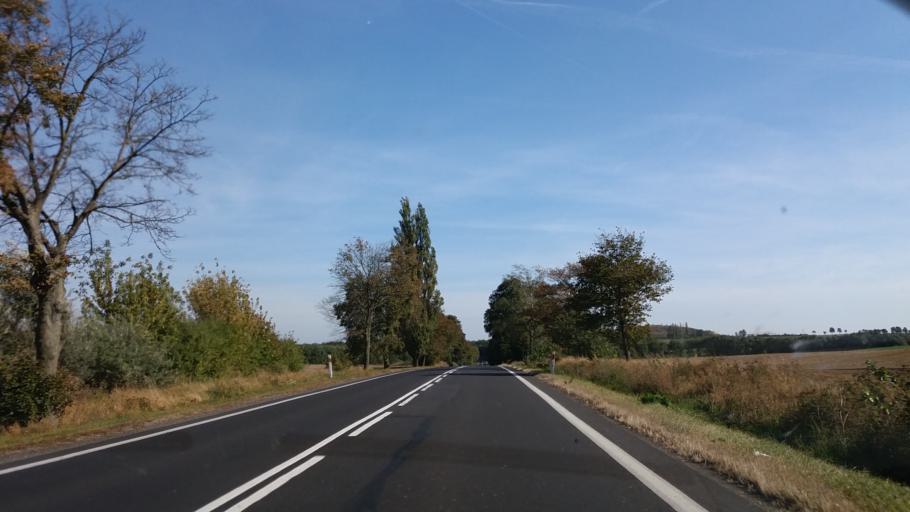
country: PL
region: Greater Poland Voivodeship
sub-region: Powiat miedzychodzki
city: Miedzychod
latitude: 52.5644
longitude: 15.9807
